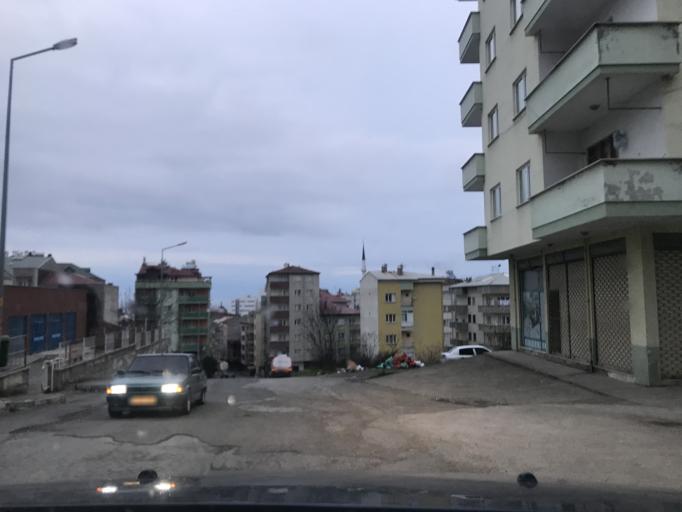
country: TR
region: Trabzon
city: Akcaabat
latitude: 41.0140
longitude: 39.5897
